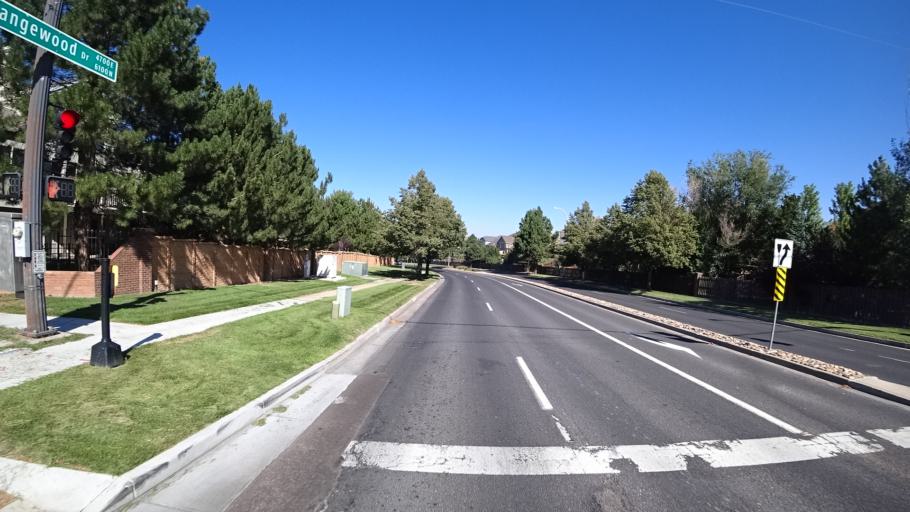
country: US
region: Colorado
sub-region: El Paso County
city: Cimarron Hills
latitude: 38.9214
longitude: -104.7422
